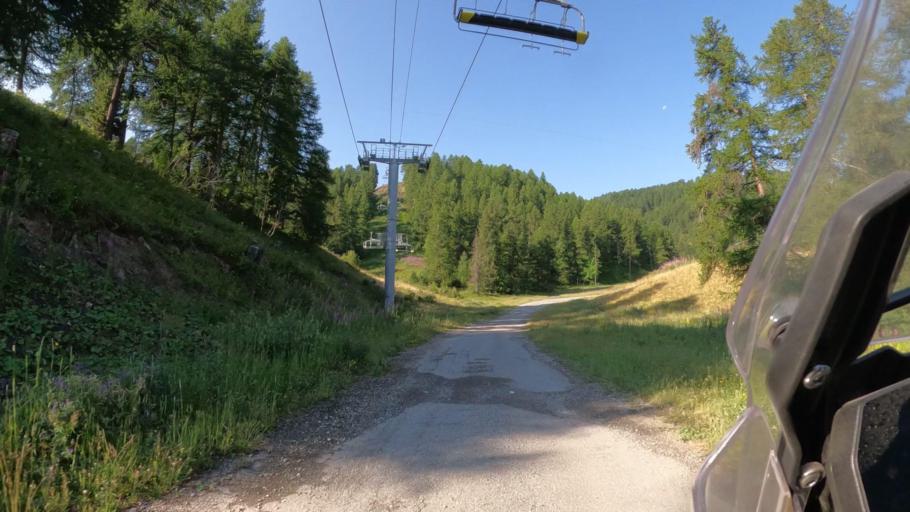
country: FR
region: Provence-Alpes-Cote d'Azur
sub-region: Departement des Hautes-Alpes
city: Guillestre
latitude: 44.6182
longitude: 6.6328
